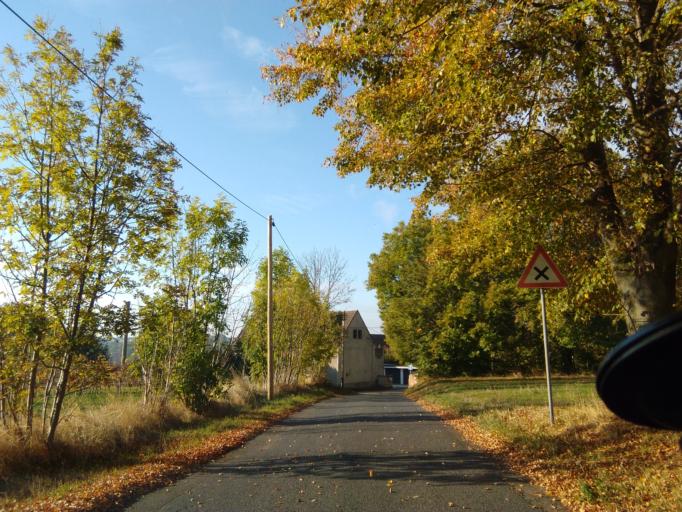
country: DE
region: Saxony
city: Meissen
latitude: 51.1832
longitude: 13.4648
